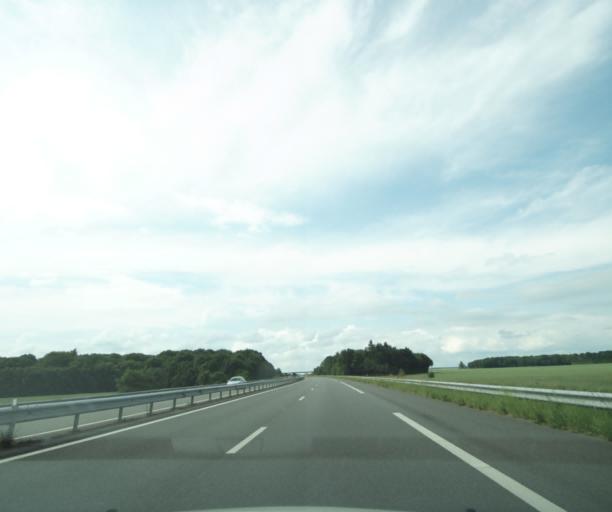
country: FR
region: Centre
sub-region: Departement du Cher
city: Levet
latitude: 46.9331
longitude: 2.4242
